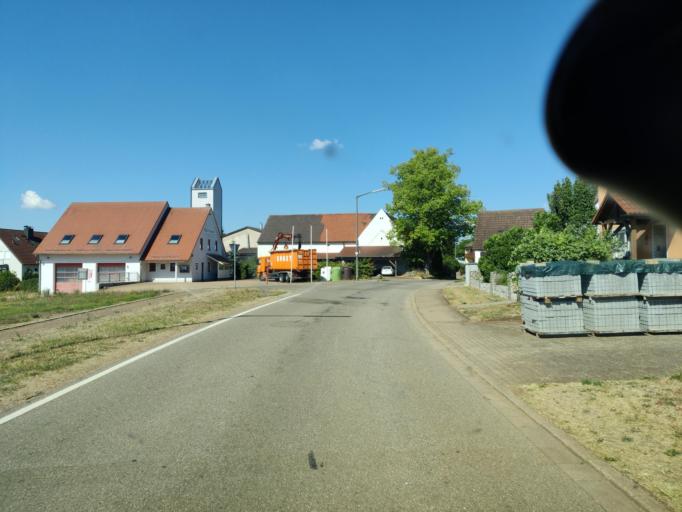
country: DE
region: Bavaria
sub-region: Regierungsbezirk Mittelfranken
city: Bergen
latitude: 49.0742
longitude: 11.1190
